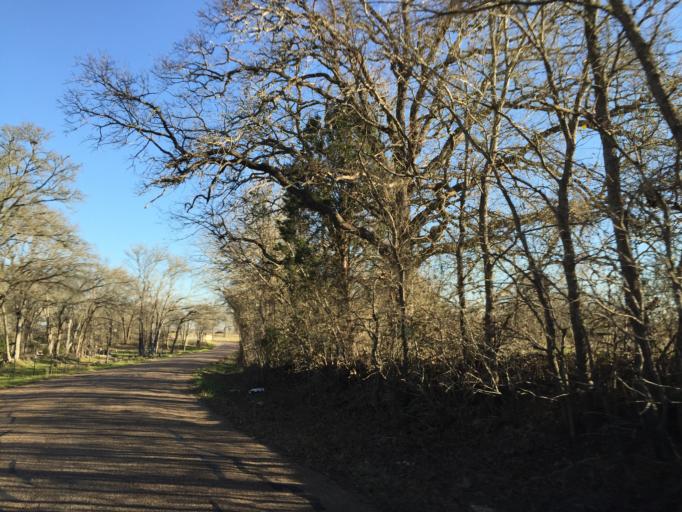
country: US
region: Texas
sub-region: Bastrop County
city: Elgin
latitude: 30.3803
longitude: -97.3089
